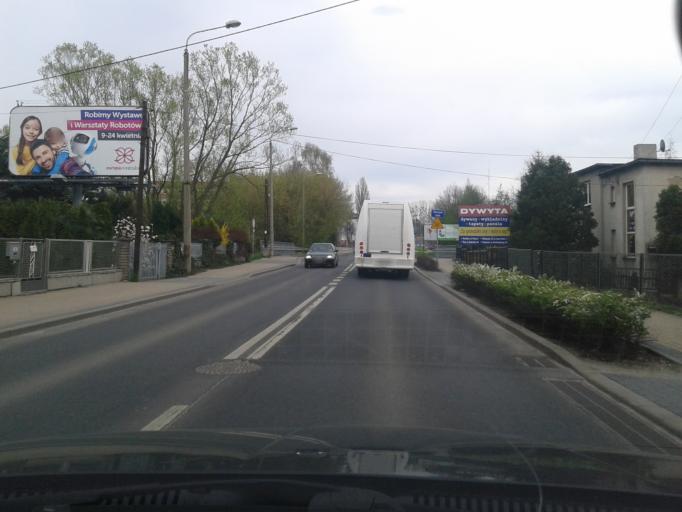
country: PL
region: Silesian Voivodeship
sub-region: Rybnik
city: Rybnik
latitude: 50.0891
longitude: 18.5381
